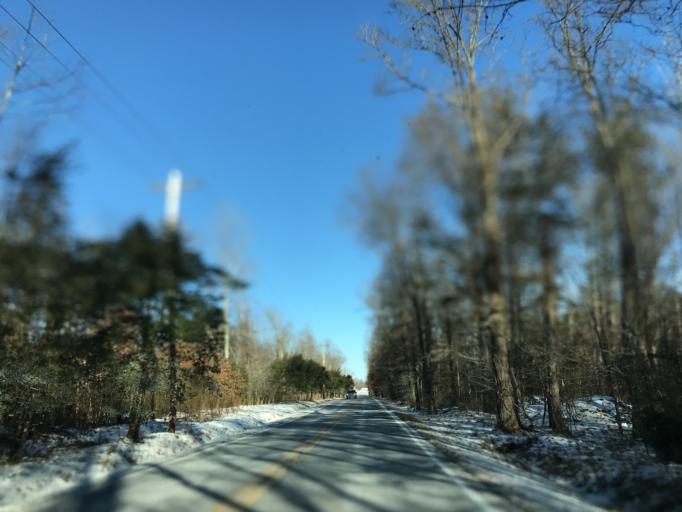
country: US
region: Maryland
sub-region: Charles County
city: La Plata
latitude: 38.4253
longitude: -76.9320
